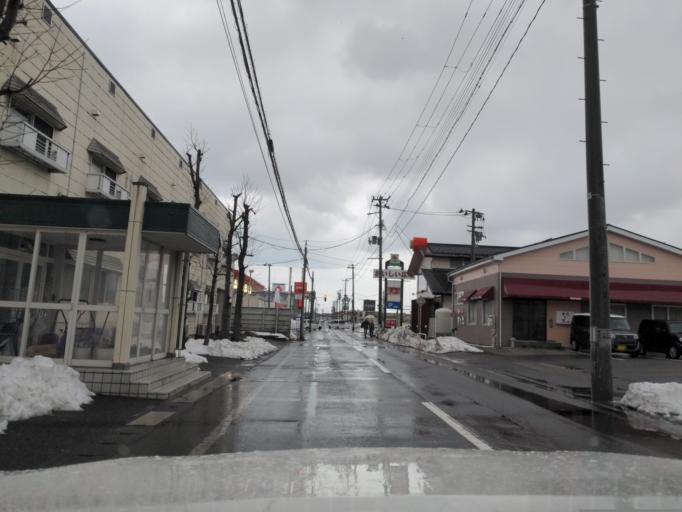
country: JP
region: Niigata
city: Kashiwazaki
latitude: 37.3595
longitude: 138.5684
